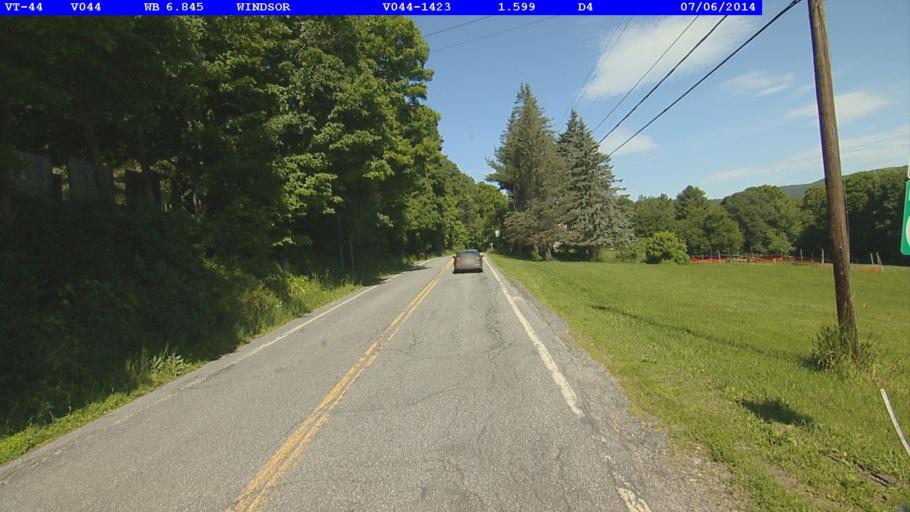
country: US
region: Vermont
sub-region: Windsor County
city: Windsor
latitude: 43.4593
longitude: -72.4244
